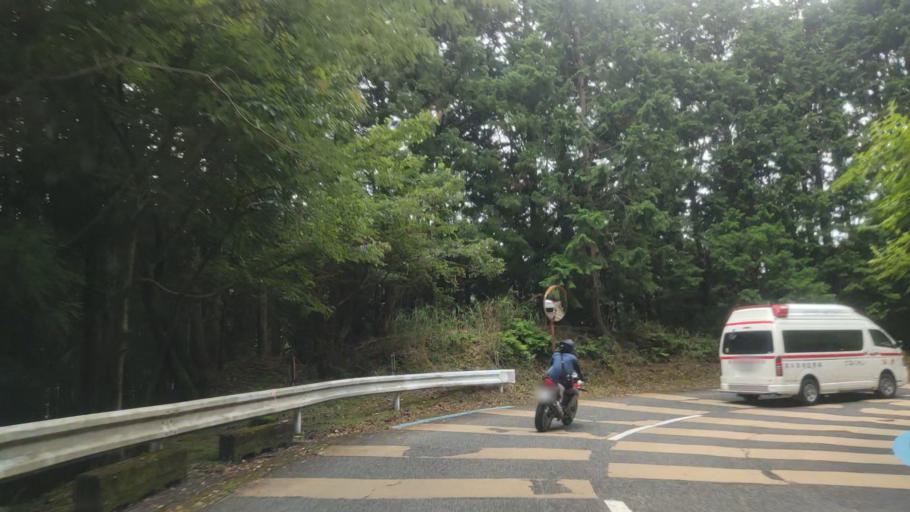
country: JP
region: Wakayama
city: Koya
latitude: 34.2223
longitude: 135.5375
